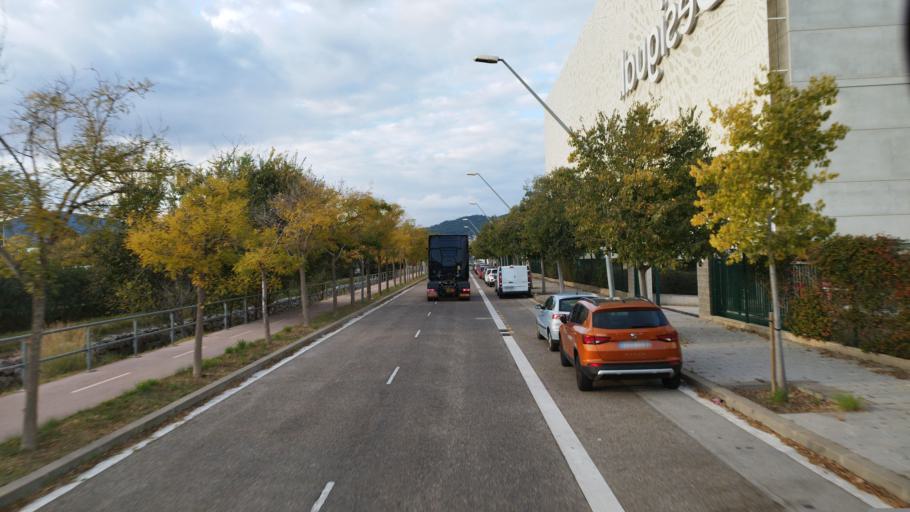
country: ES
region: Catalonia
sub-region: Provincia de Barcelona
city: Viladecans
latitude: 41.3008
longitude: 2.0198
